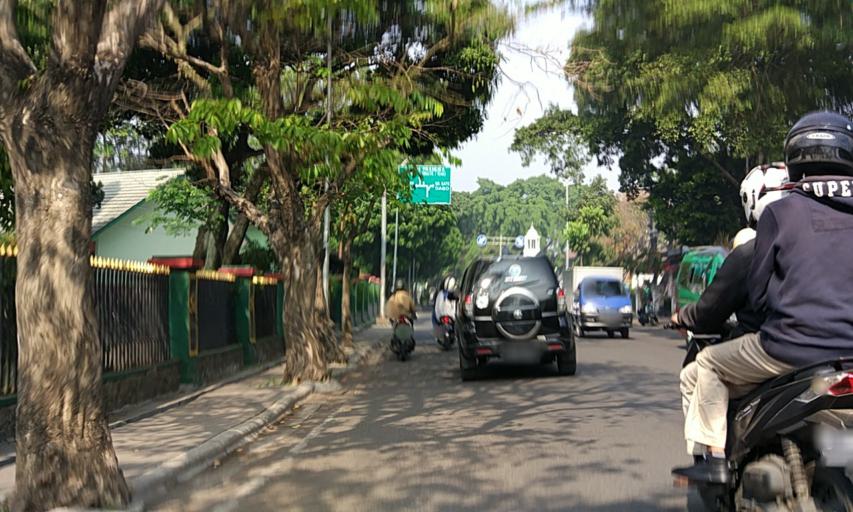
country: ID
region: West Java
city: Bandung
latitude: -6.9058
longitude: 107.6308
